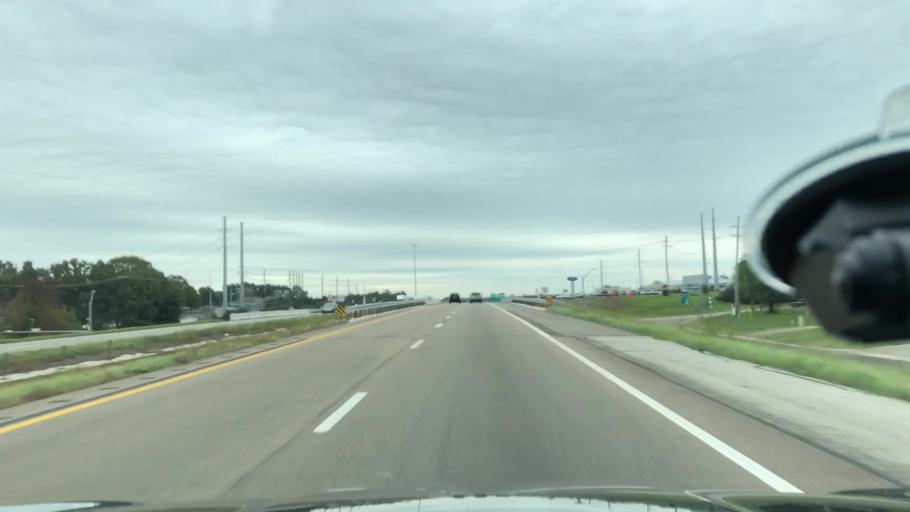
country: US
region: Texas
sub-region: Titus County
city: Mount Pleasant
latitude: 33.1742
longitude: -94.9849
